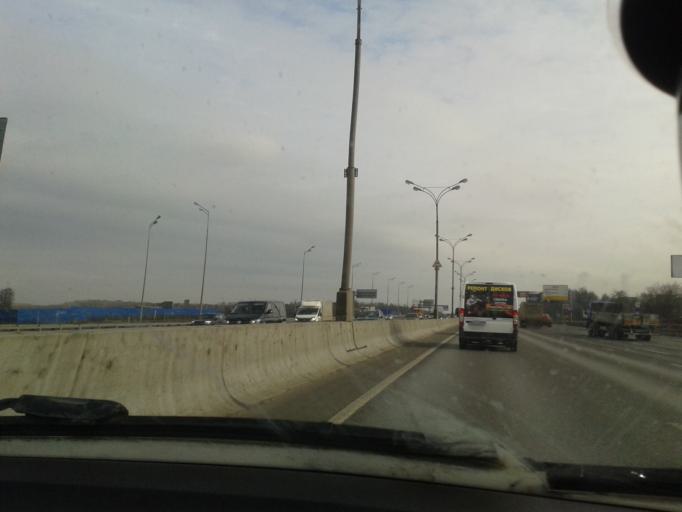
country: RU
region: Moscow
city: Businovo
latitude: 55.8931
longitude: 37.4989
